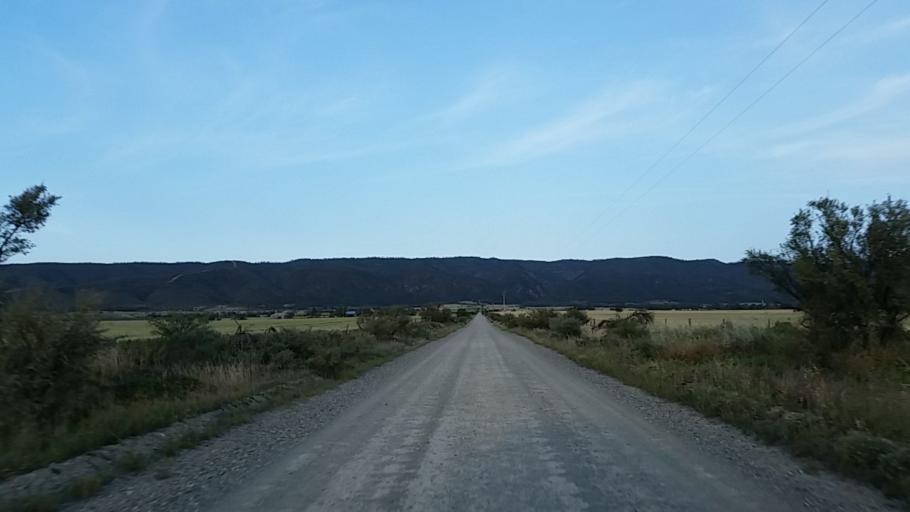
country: AU
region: South Australia
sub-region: Port Pirie City and Dists
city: Port Pirie
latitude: -33.0547
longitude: 138.0778
